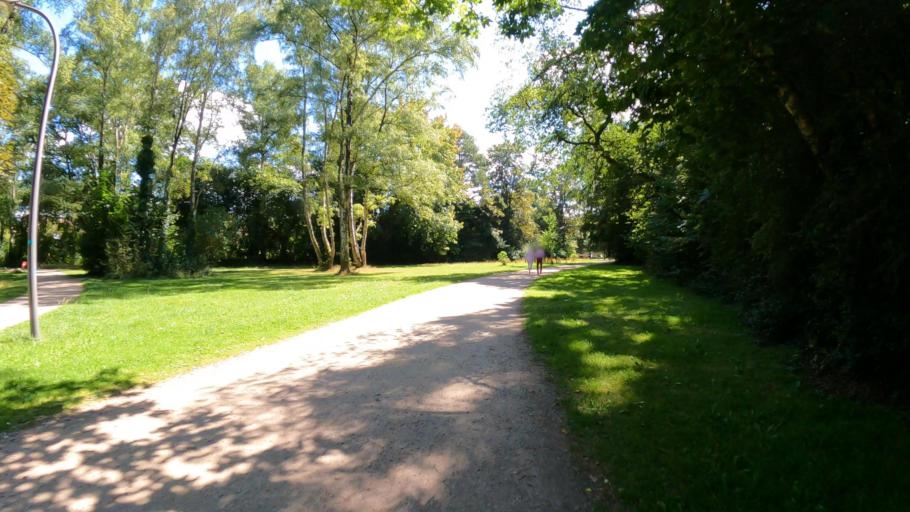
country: DE
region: Hamburg
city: Langenhorn
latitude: 53.6727
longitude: 10.0222
